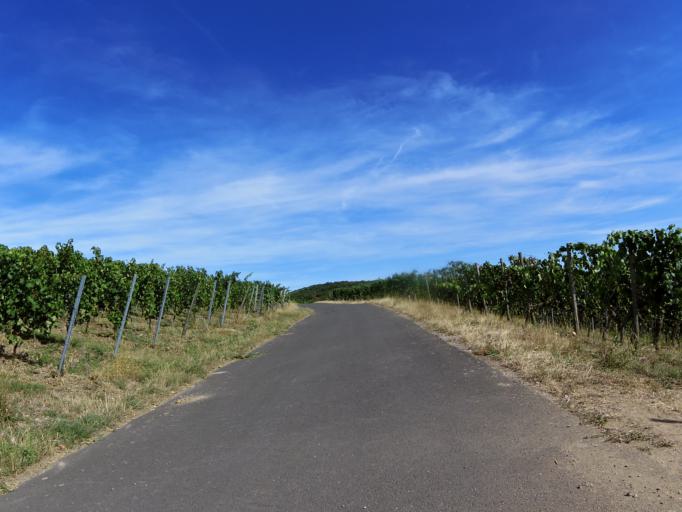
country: DE
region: Bavaria
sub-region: Regierungsbezirk Unterfranken
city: Eibelstadt
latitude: 49.7415
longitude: 10.0018
